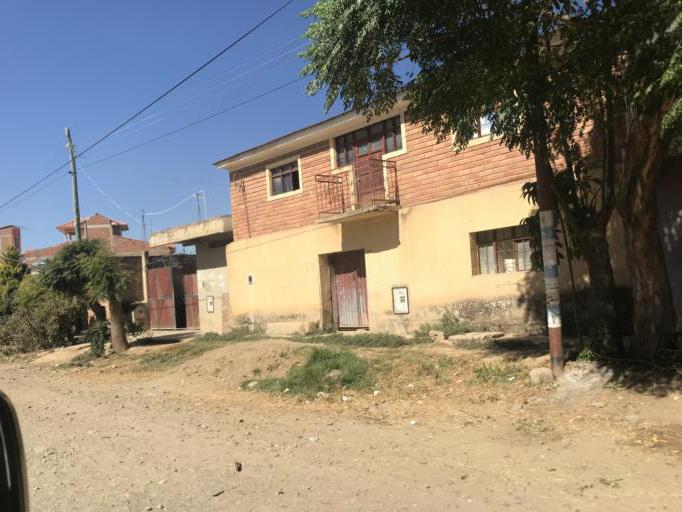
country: BO
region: Cochabamba
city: Cliza
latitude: -17.5841
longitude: -65.9166
